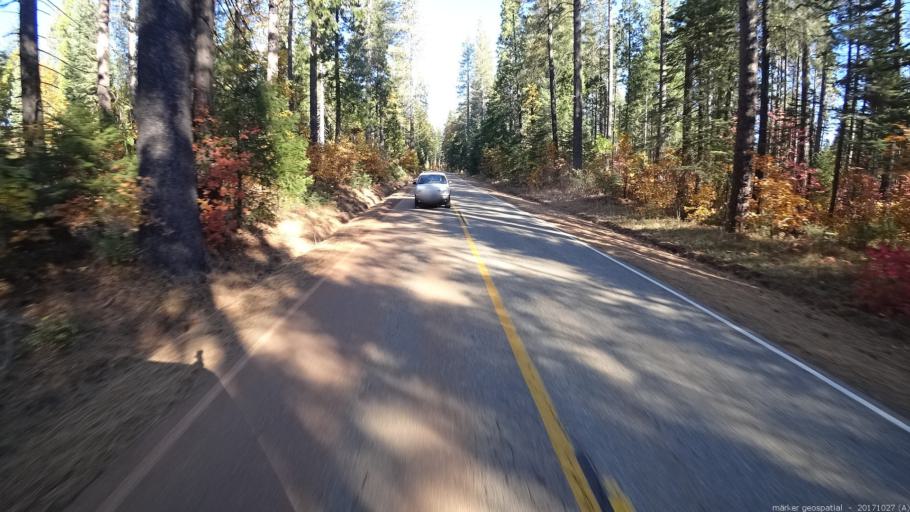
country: US
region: California
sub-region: Shasta County
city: Burney
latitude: 40.9371
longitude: -121.9490
